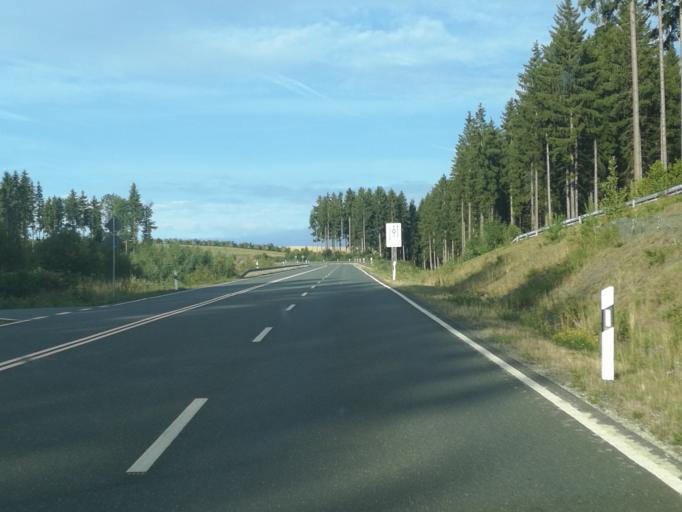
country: DE
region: Saxony
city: Adorf
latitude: 50.3405
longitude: 12.2427
